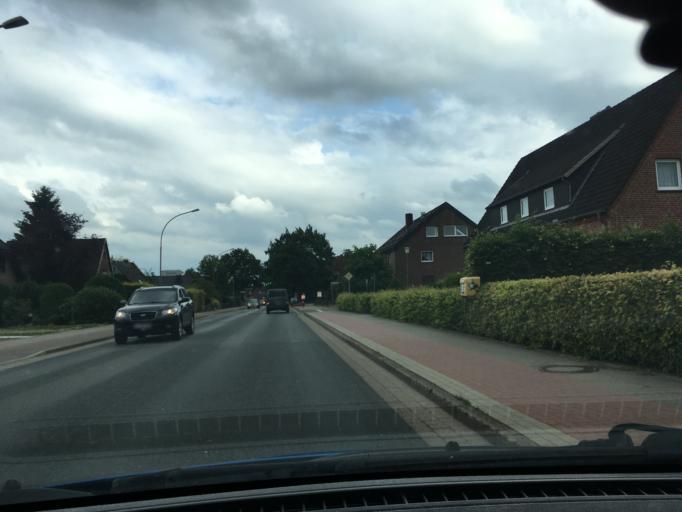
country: DE
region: Lower Saxony
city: Tostedt
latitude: 53.2741
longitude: 9.7194
